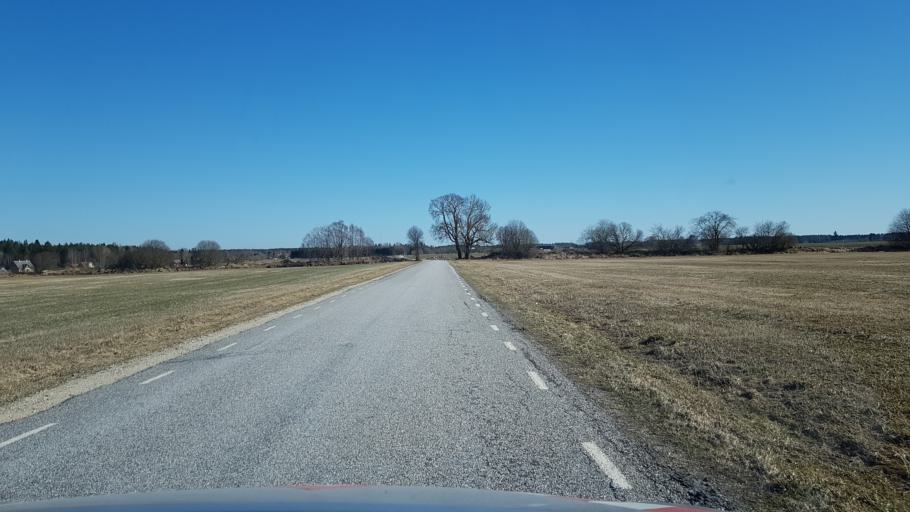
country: EE
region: Laeaene-Virumaa
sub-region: Viru-Nigula vald
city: Kunda
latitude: 59.4033
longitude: 26.5437
